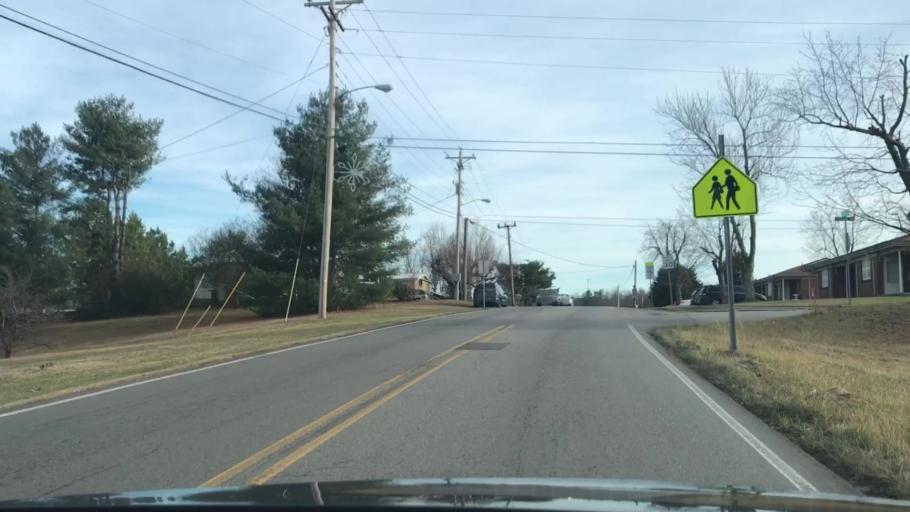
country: US
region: Tennessee
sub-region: Putnam County
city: Monterey
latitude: 36.1378
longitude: -85.2640
